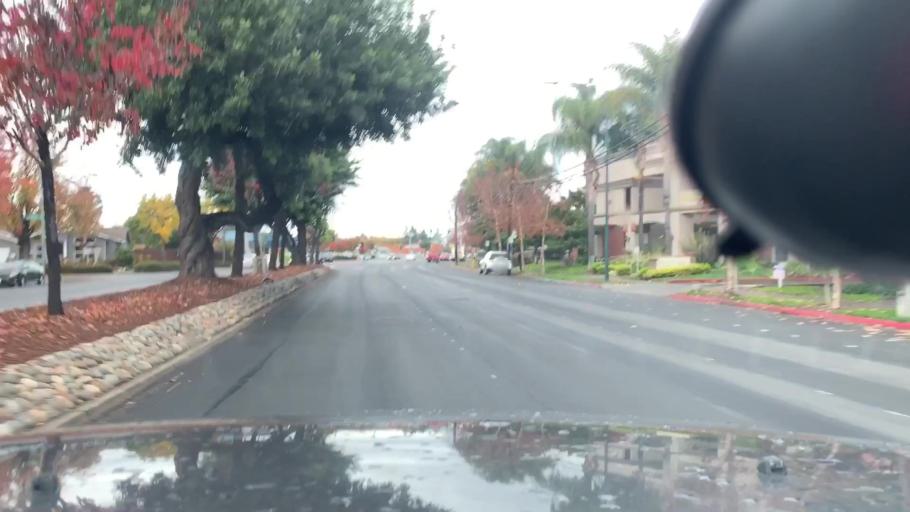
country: US
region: California
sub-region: Santa Clara County
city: Campbell
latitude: 37.3131
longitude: -121.9772
